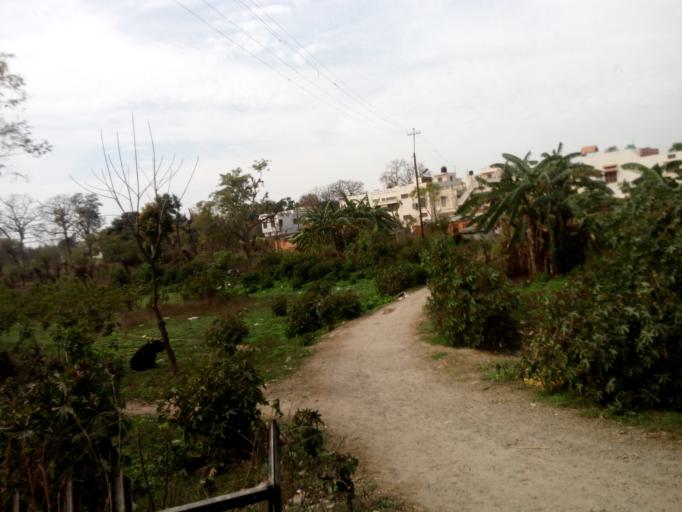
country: IN
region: Punjab
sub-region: Hoshiarpur
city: Hoshiarpur
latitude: 31.5228
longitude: 75.9018
